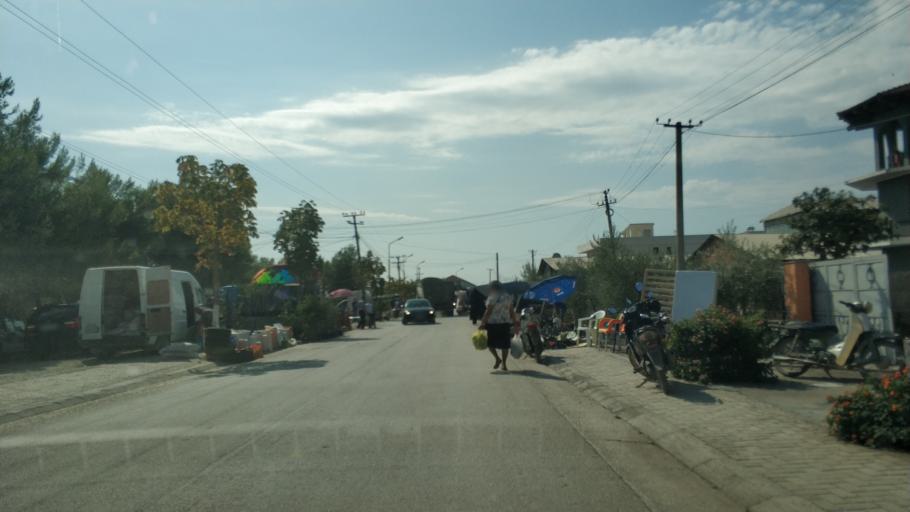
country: AL
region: Fier
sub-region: Rrethi i Lushnjes
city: Divjake
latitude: 40.9931
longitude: 19.5334
